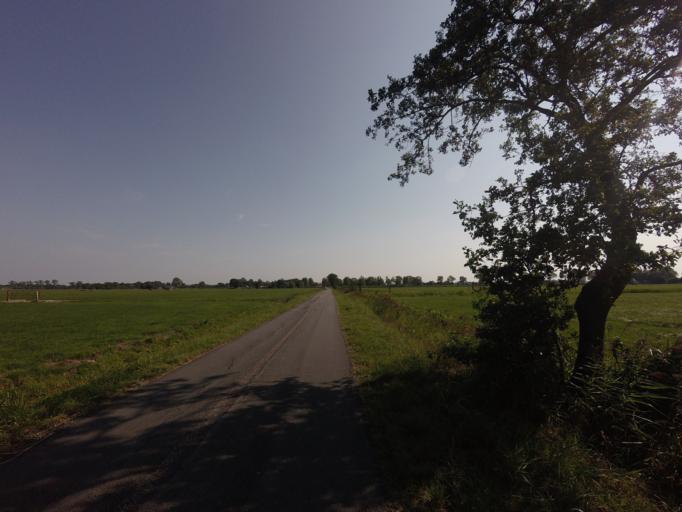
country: NL
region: Groningen
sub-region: Gemeente Zuidhorn
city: Zuidhorn
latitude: 53.2141
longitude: 6.4325
